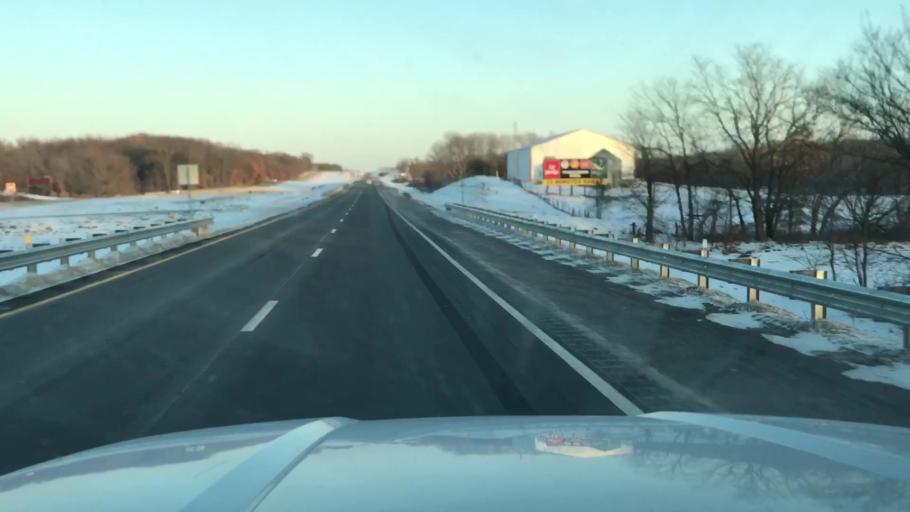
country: US
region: Missouri
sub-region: DeKalb County
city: Maysville
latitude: 39.7620
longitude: -94.4855
